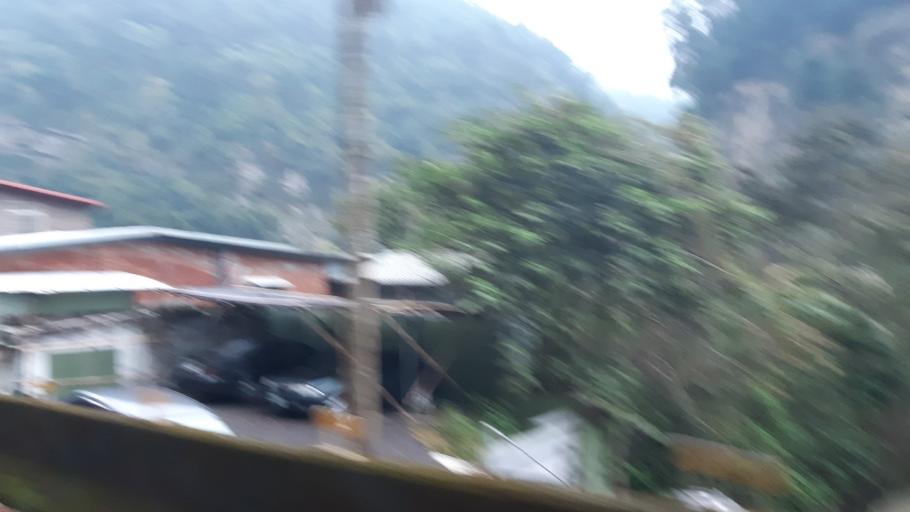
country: TW
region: Taiwan
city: Daxi
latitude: 24.6889
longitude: 121.2188
